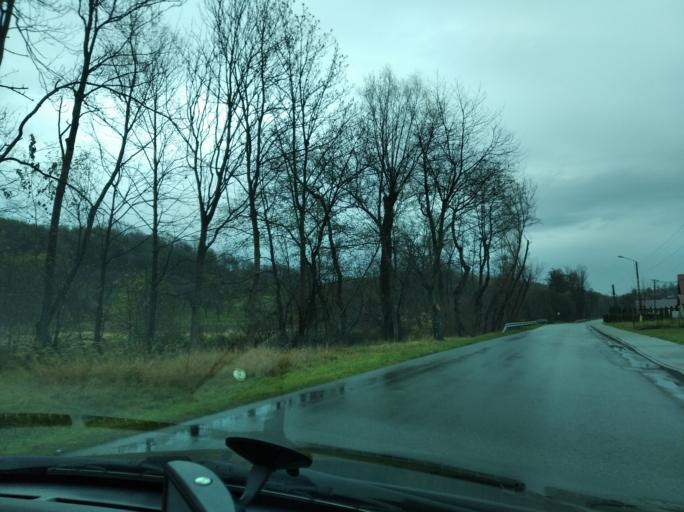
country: PL
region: Subcarpathian Voivodeship
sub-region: Powiat rzeszowski
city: Straszydle
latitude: 49.9145
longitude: 21.9585
